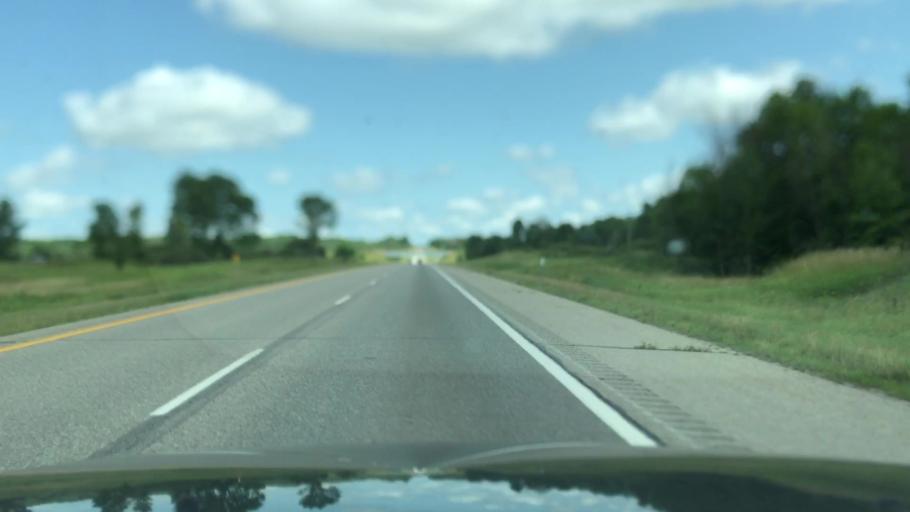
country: US
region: Michigan
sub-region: Mecosta County
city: Big Rapids
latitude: 43.7102
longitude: -85.5292
